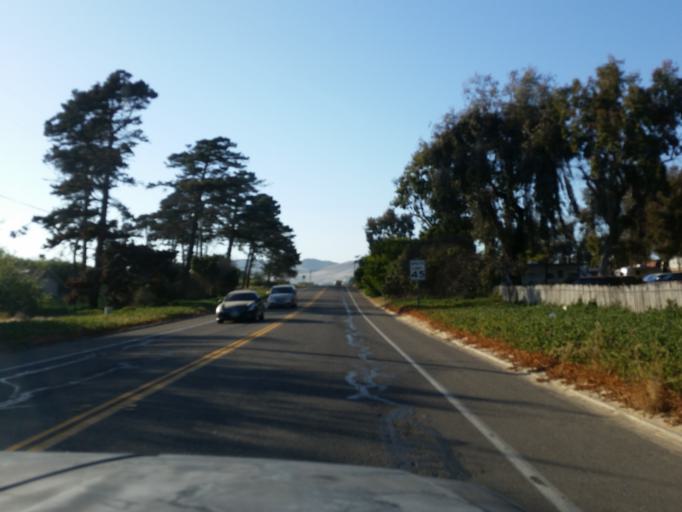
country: US
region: California
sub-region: San Luis Obispo County
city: Grover Beach
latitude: 35.1137
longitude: -120.6263
